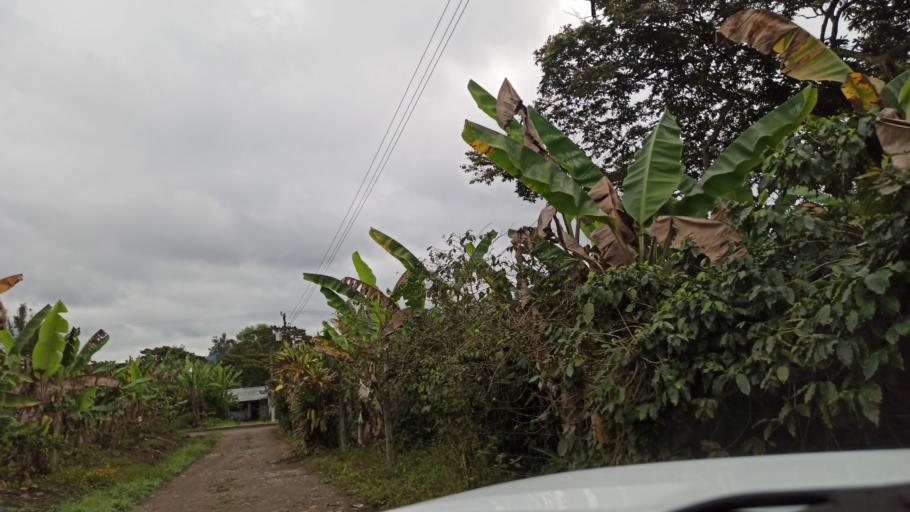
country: MX
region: Veracruz
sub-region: Chocaman
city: San Jose Neria
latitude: 18.9935
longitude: -97.0000
